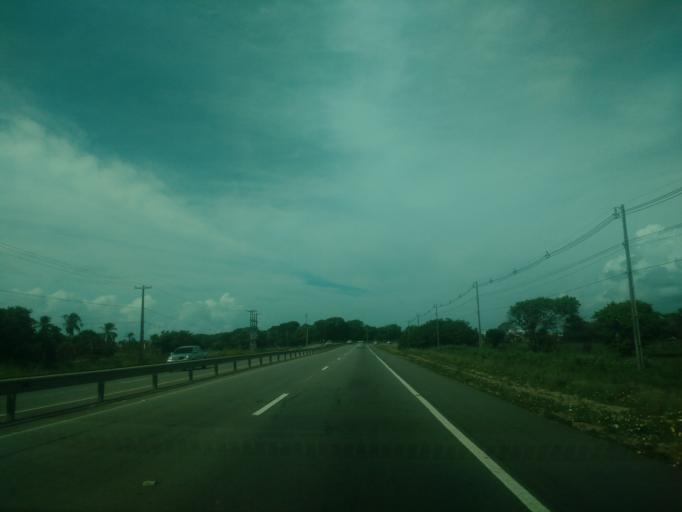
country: BR
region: Alagoas
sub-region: Marechal Deodoro
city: Marechal Deodoro
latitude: -9.7619
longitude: -35.8446
